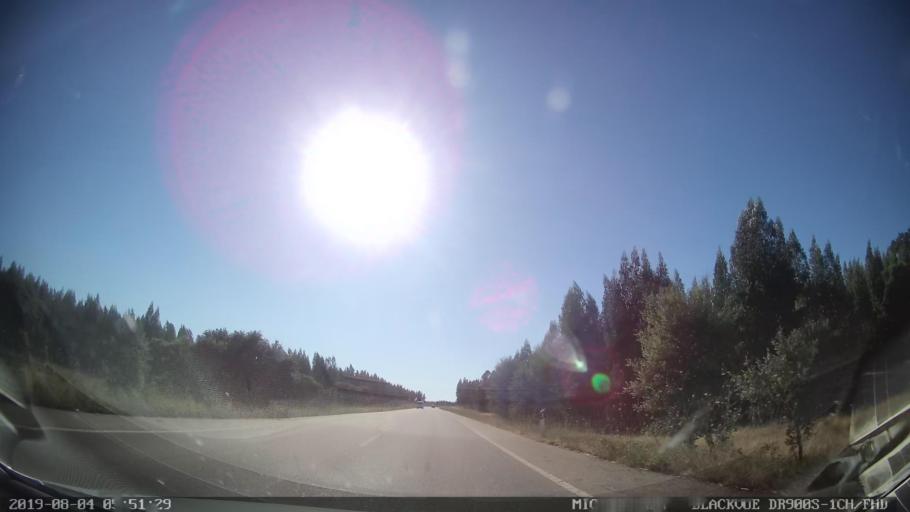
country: PT
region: Portalegre
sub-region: Gaviao
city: Gaviao
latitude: 39.4466
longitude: -7.8931
